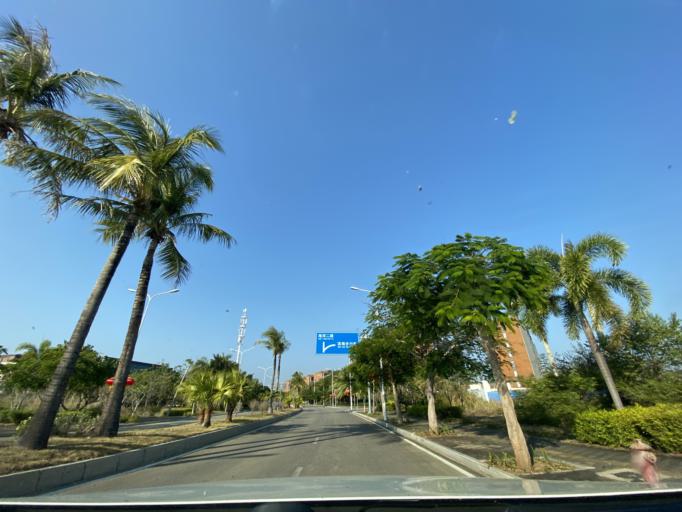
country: CN
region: Hainan
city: Haitangwan
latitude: 18.4052
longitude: 109.7802
